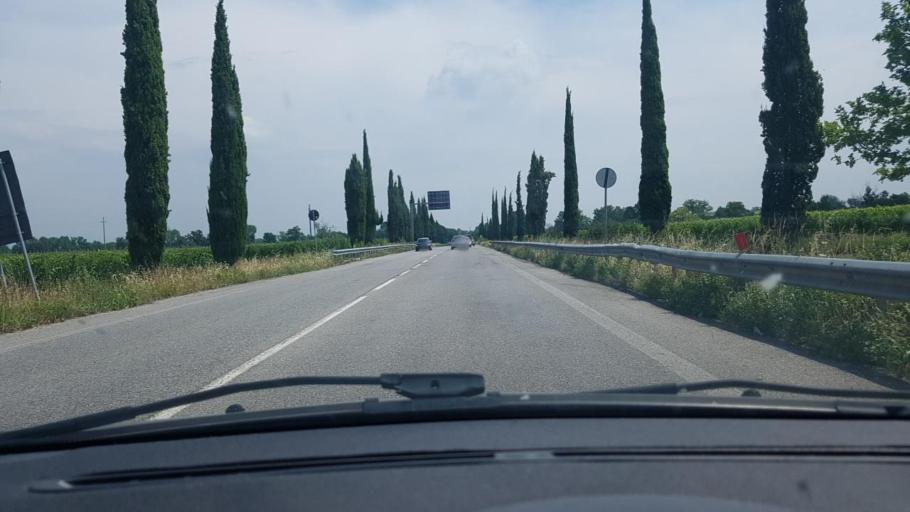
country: IT
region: Lombardy
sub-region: Provincia di Brescia
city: San Martino della Battaglia
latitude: 45.4440
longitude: 10.6232
